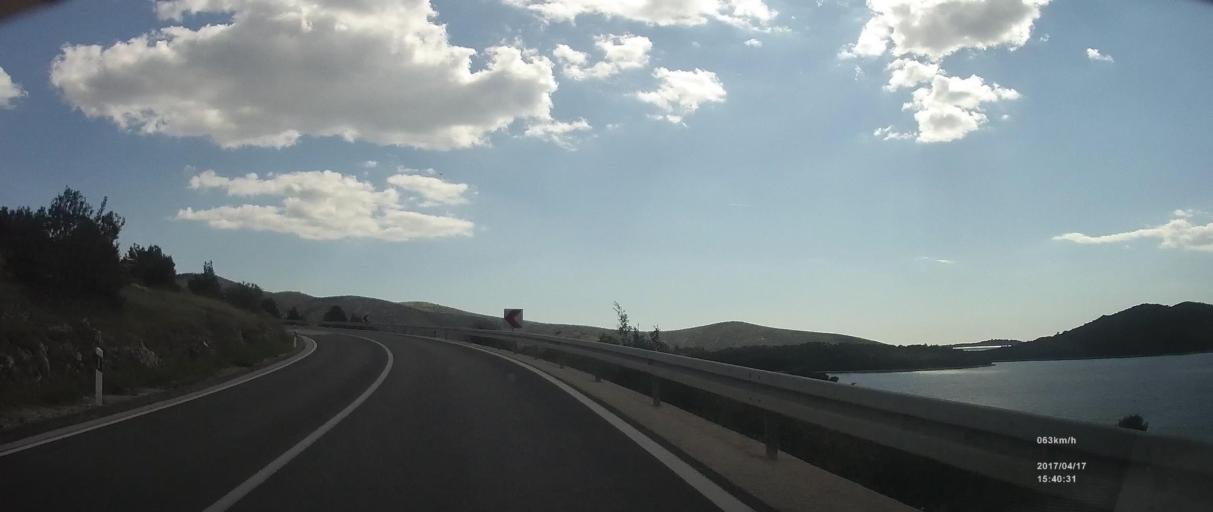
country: HR
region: Sibensko-Kniniska
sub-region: Grad Sibenik
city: Brodarica
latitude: 43.6482
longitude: 15.9508
